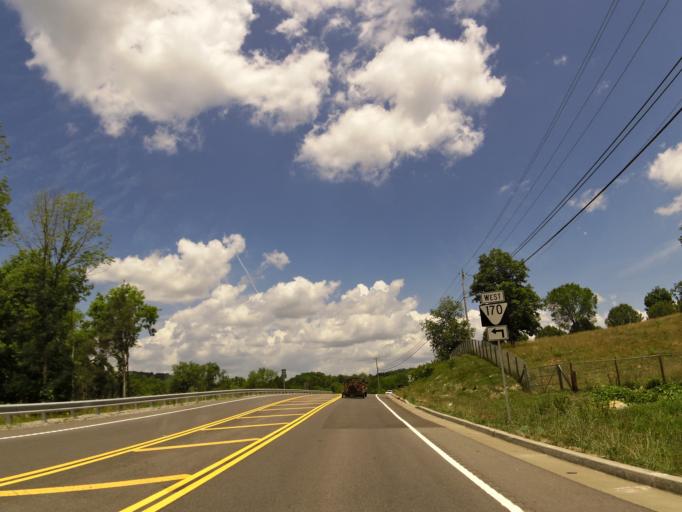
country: US
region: Tennessee
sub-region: Union County
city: Maynardville
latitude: 36.3048
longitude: -83.7599
